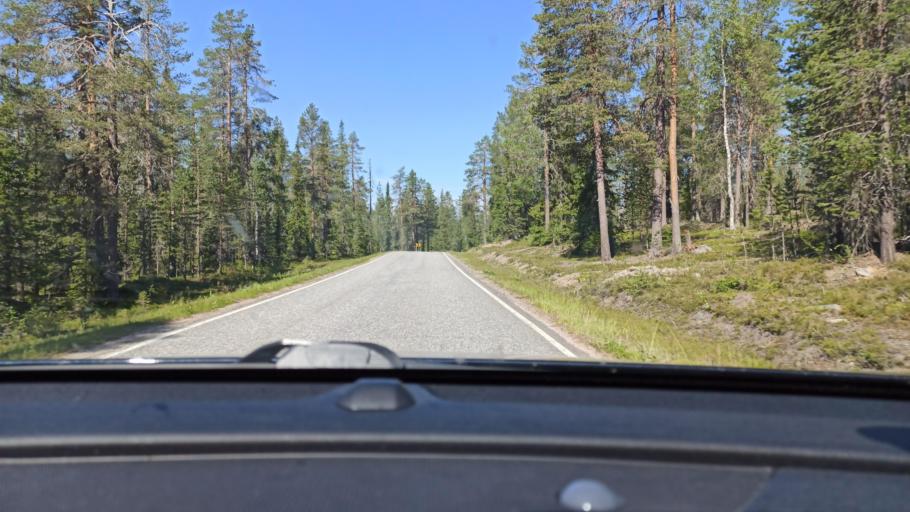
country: FI
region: Lapland
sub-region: Tunturi-Lappi
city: Kolari
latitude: 67.6702
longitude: 24.1528
